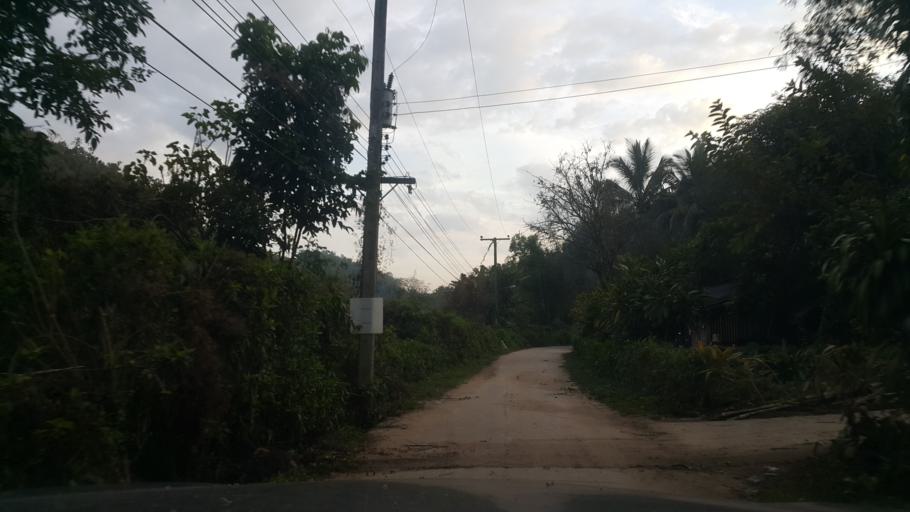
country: TH
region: Chiang Mai
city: Samoeng
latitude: 19.0048
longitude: 98.6721
